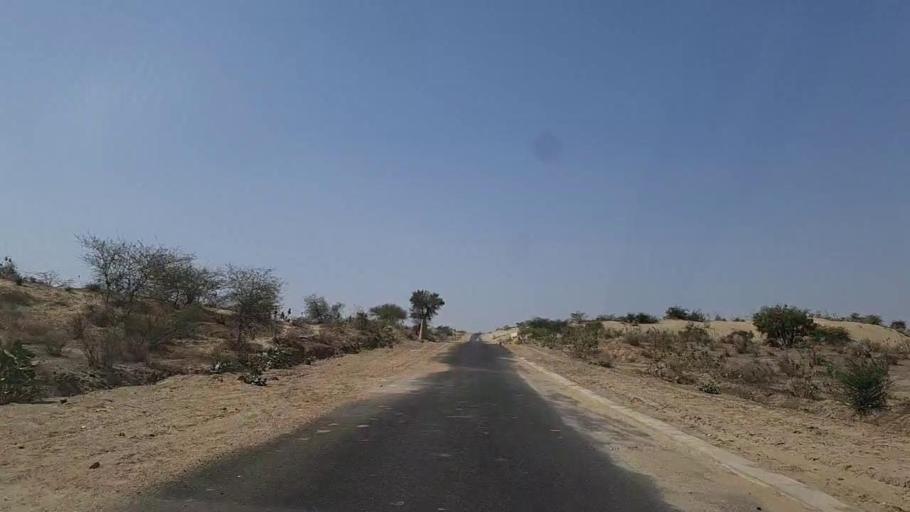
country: PK
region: Sindh
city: Diplo
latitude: 24.5600
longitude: 69.4564
